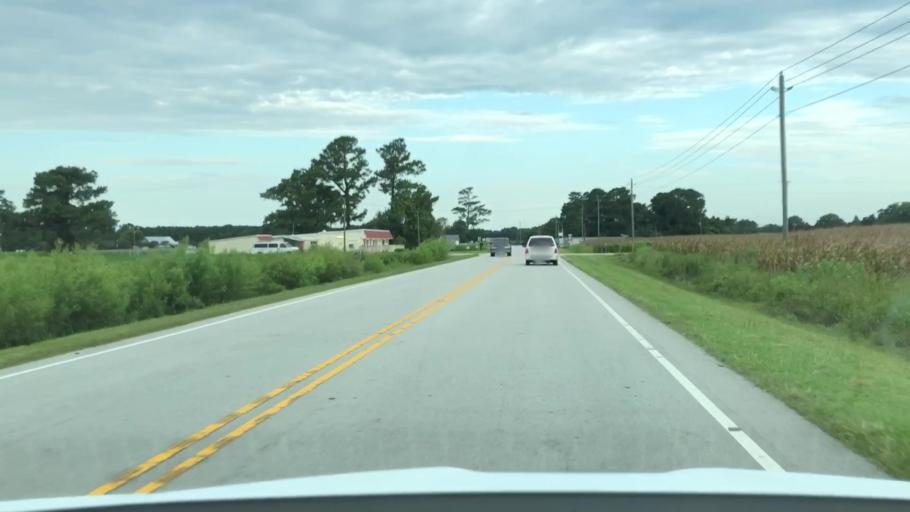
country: US
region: North Carolina
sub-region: Jones County
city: Trenton
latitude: 35.0781
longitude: -77.3982
